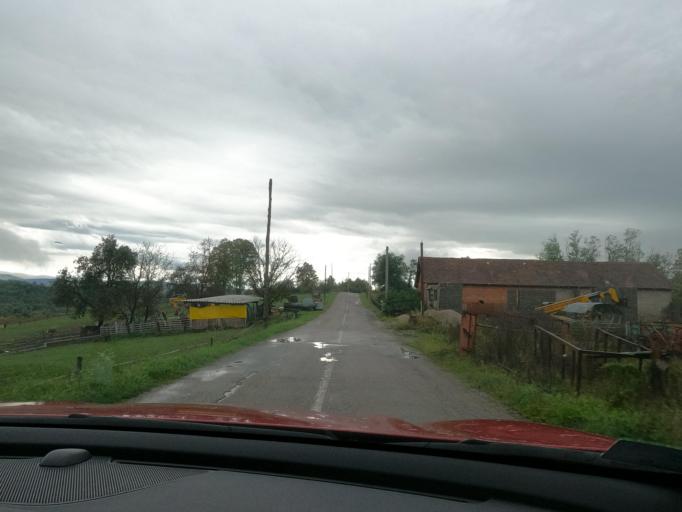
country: HR
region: Sisacko-Moslavacka
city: Glina
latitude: 45.3013
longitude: 16.1682
